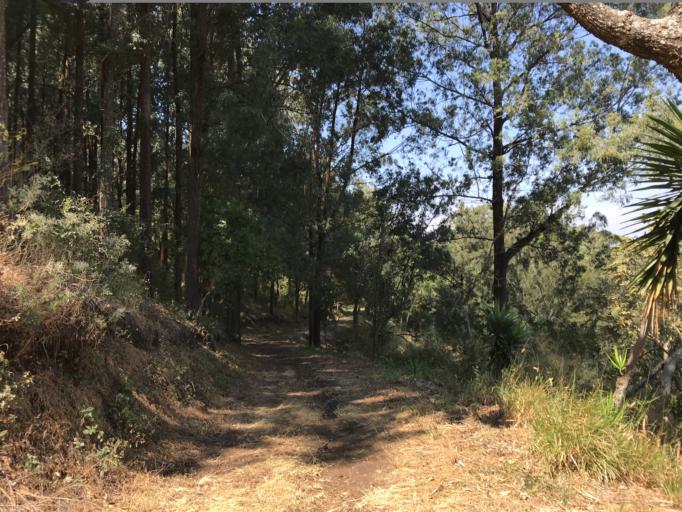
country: GT
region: Guatemala
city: Villa Canales
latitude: 14.4810
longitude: -90.5451
